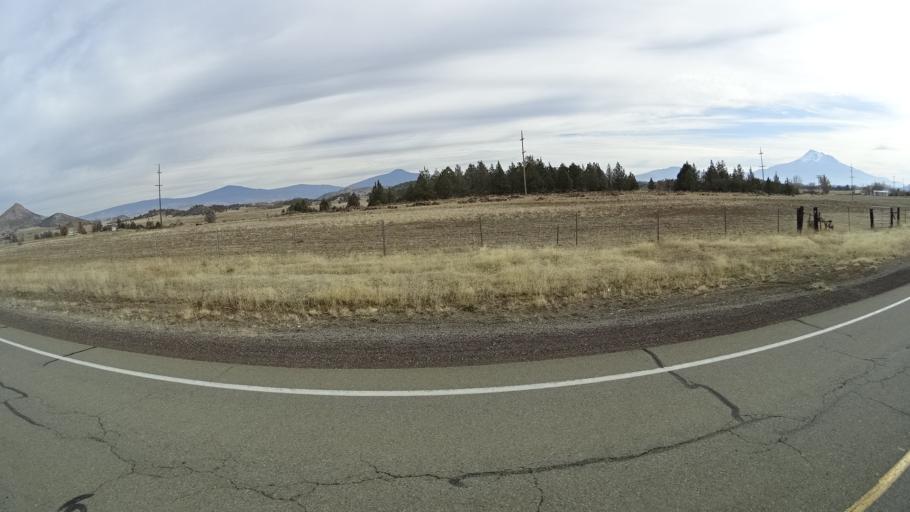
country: US
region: California
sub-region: Siskiyou County
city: Montague
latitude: 41.6870
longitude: -122.5354
